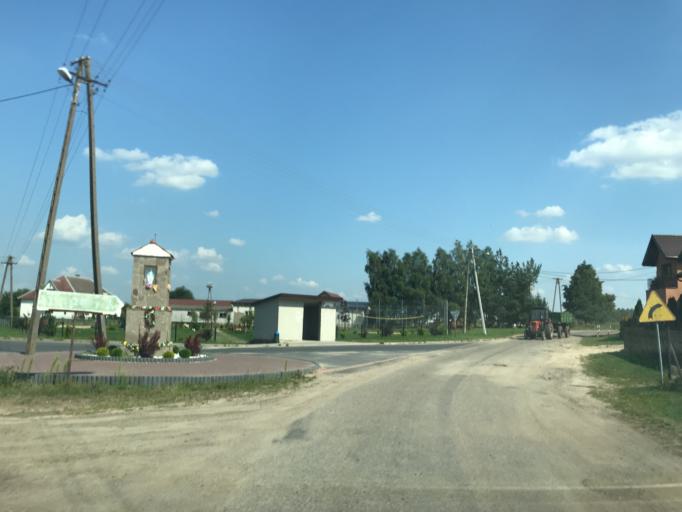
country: PL
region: Masovian Voivodeship
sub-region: Powiat zurominski
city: Lubowidz
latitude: 53.1732
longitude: 19.8996
